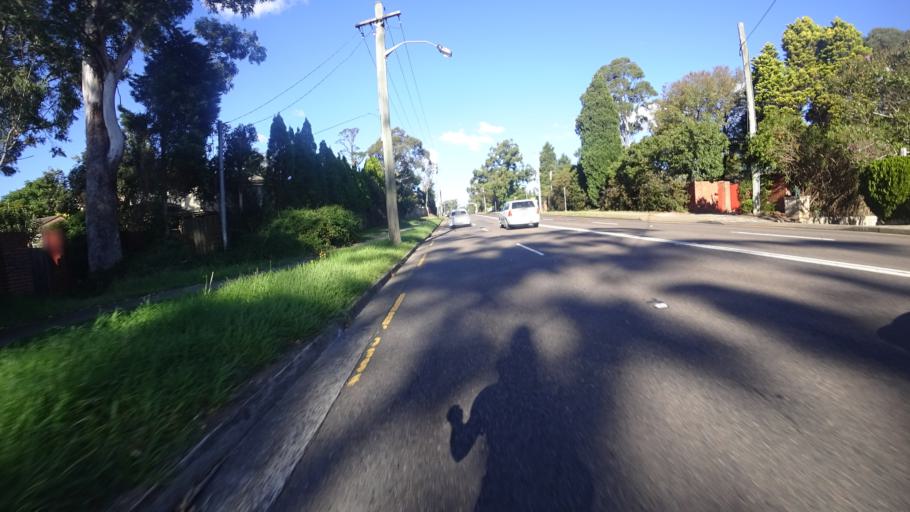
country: AU
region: New South Wales
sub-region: The Hills Shire
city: West Pennant
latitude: -33.7344
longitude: 151.0290
